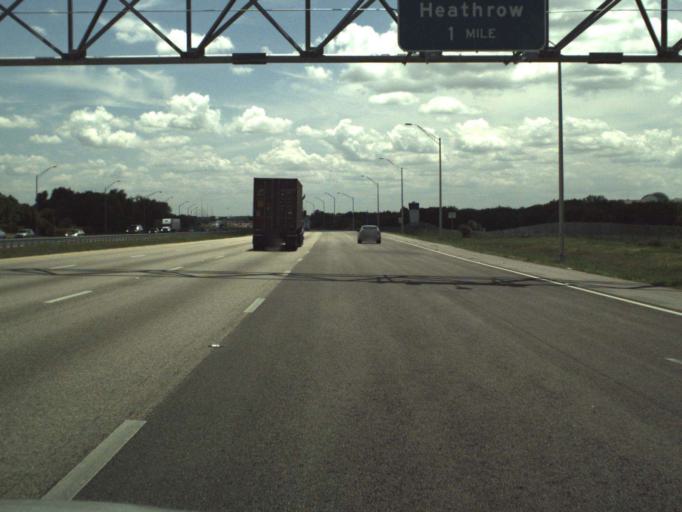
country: US
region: Florida
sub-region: Seminole County
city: Heathrow
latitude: 28.7747
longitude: -81.3566
